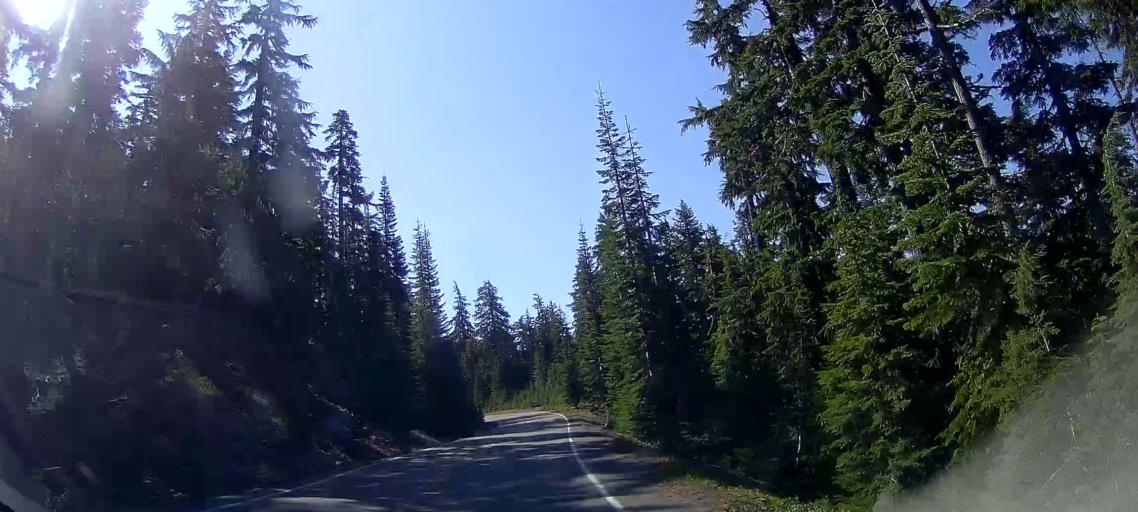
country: US
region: Oregon
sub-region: Klamath County
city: Klamath Falls
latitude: 42.8805
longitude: -122.1238
